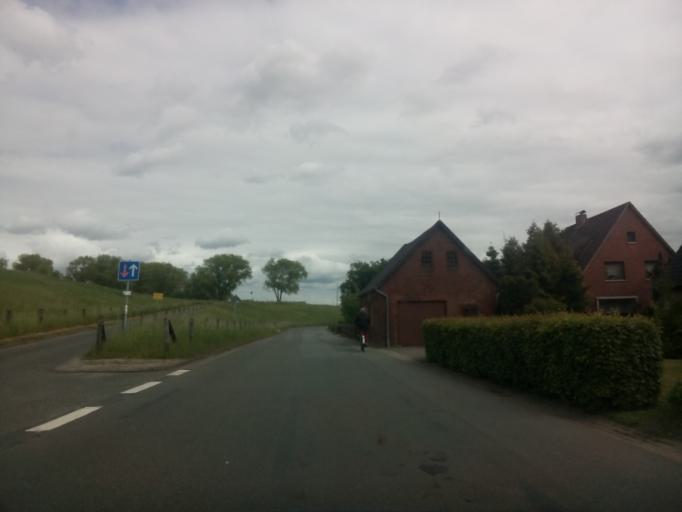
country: DE
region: Lower Saxony
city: Lemwerder
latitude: 53.1671
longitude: 8.5829
